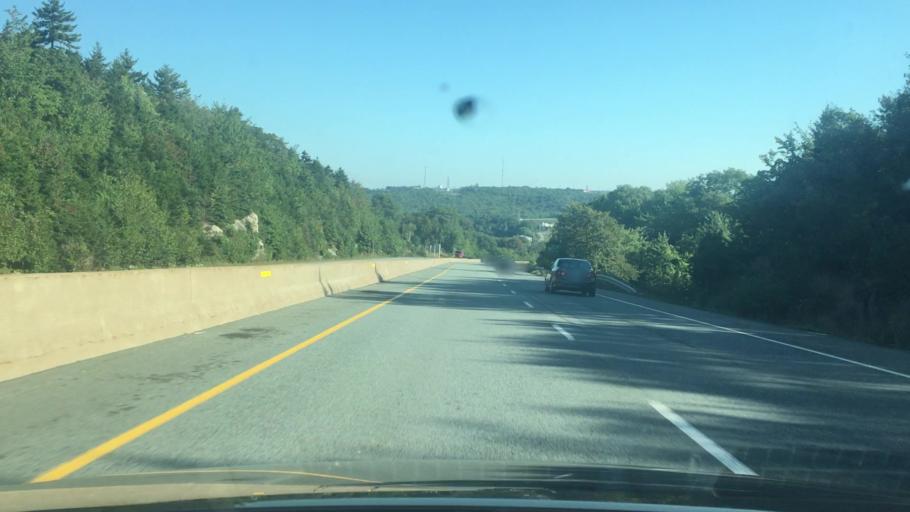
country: CA
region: Nova Scotia
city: Dartmouth
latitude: 44.7373
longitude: -63.6616
